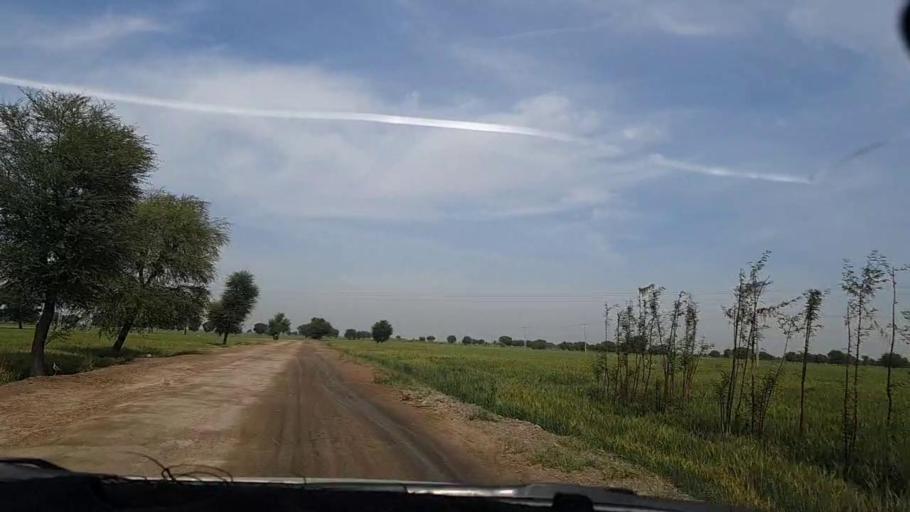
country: PK
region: Sindh
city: Dhoro Naro
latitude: 25.4483
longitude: 69.4973
